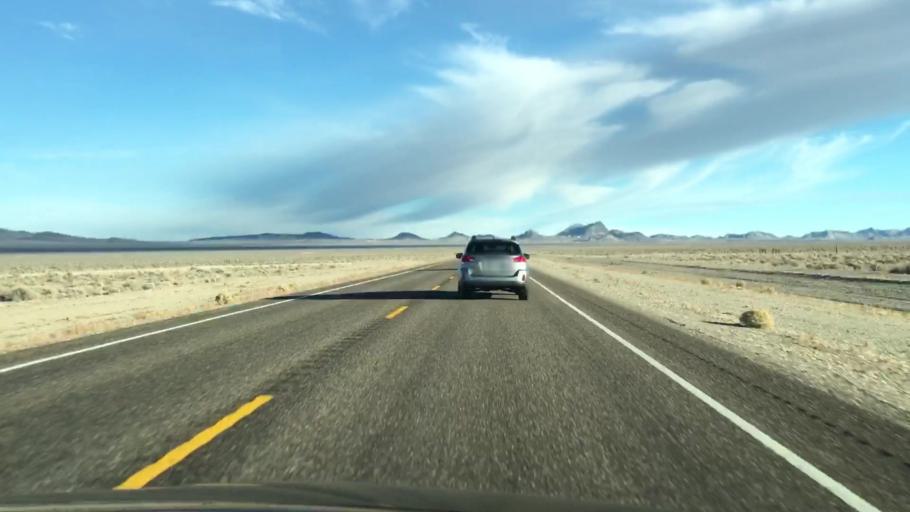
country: US
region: Nevada
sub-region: Nye County
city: Tonopah
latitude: 38.1234
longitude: -117.4018
